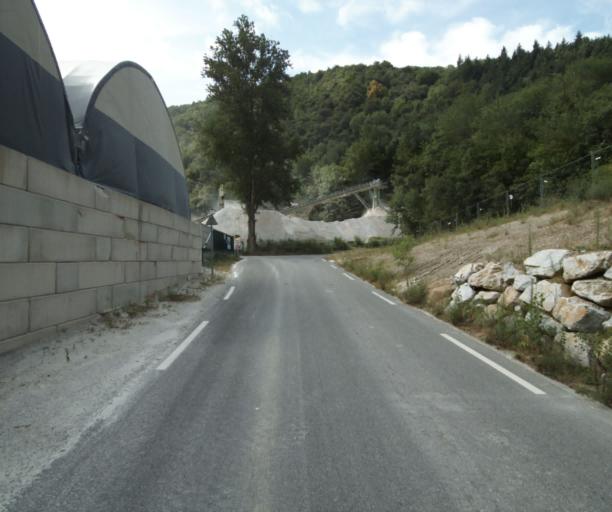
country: FR
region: Midi-Pyrenees
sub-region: Departement du Tarn
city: Soreze
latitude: 43.4552
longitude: 2.1079
